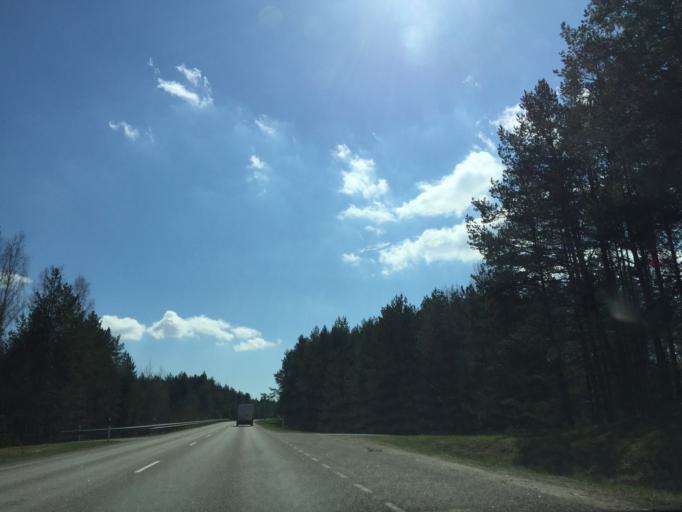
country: EE
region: Tartu
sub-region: Elva linn
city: Elva
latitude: 58.0693
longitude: 26.2033
